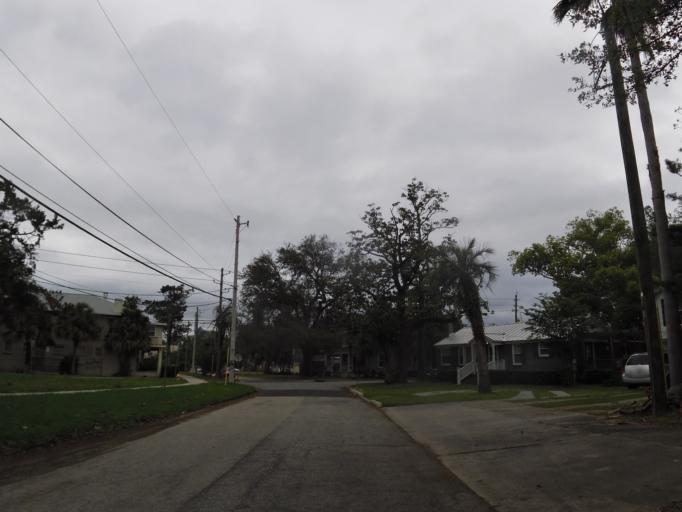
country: US
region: Florida
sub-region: Duval County
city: Jacksonville
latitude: 30.3064
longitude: -81.6554
